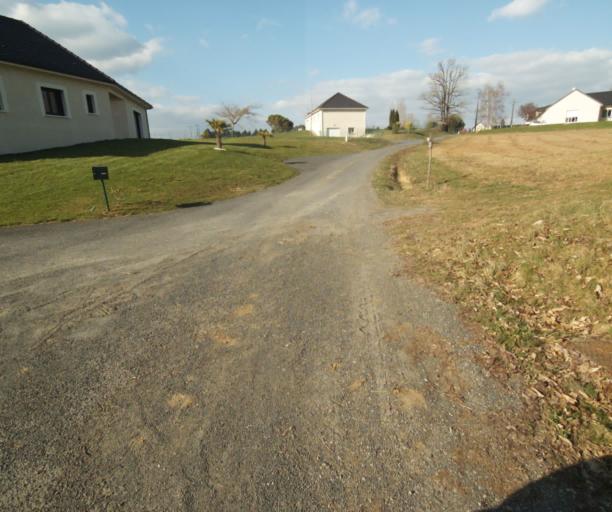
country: FR
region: Limousin
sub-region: Departement de la Correze
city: Saint-Clement
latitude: 45.3482
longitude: 1.6319
